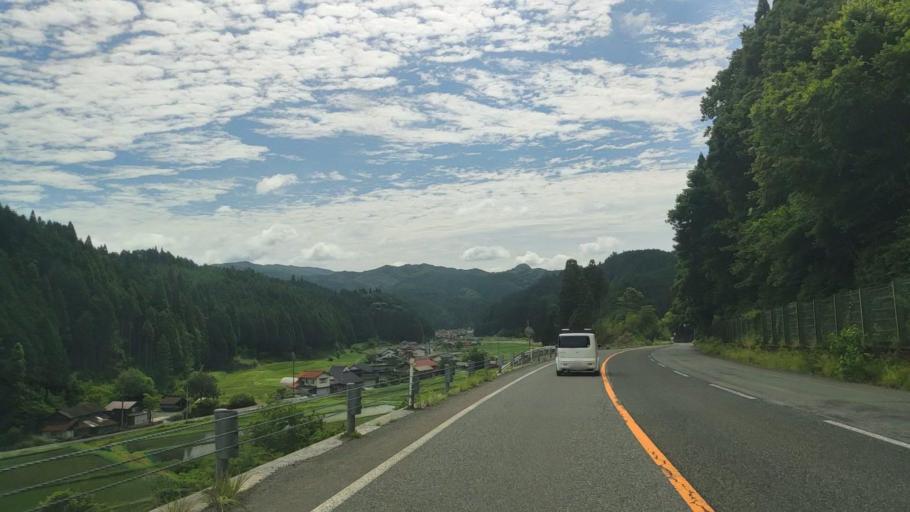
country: JP
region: Okayama
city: Niimi
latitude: 35.1795
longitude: 133.5554
